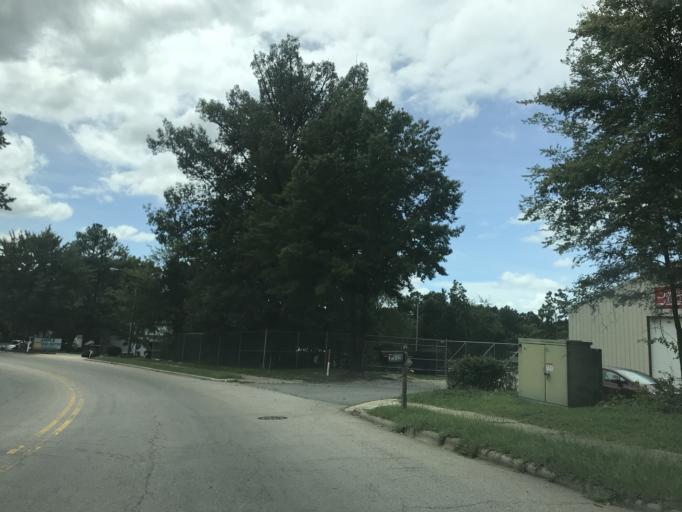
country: US
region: North Carolina
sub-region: Wake County
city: Raleigh
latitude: 35.7941
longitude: -78.5692
